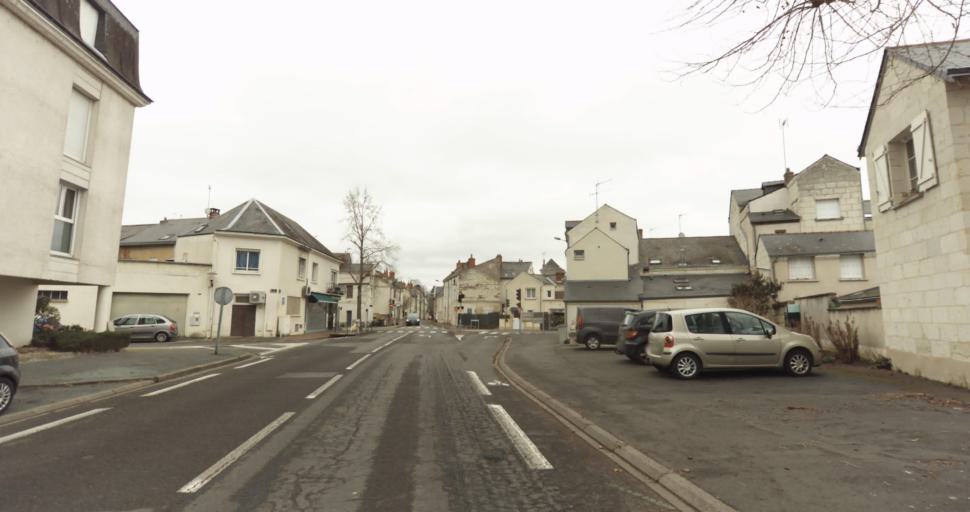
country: FR
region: Pays de la Loire
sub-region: Departement de Maine-et-Loire
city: Saumur
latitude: 47.2527
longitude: -0.0790
